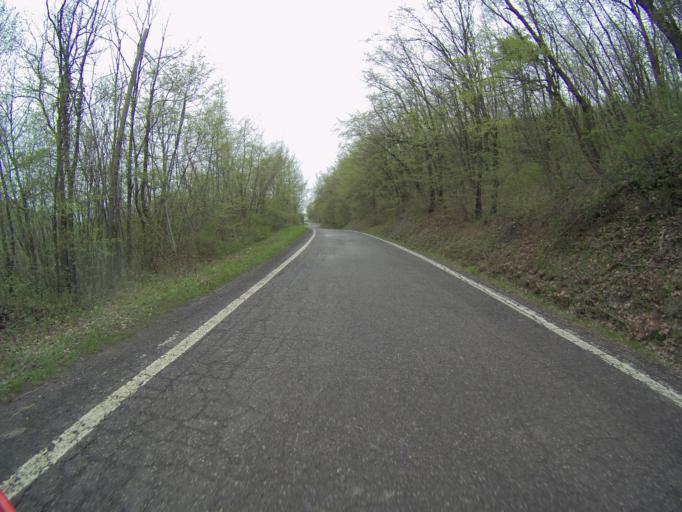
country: IT
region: Emilia-Romagna
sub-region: Provincia di Reggio Emilia
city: San Polo d'Enza
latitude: 44.6051
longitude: 10.4441
